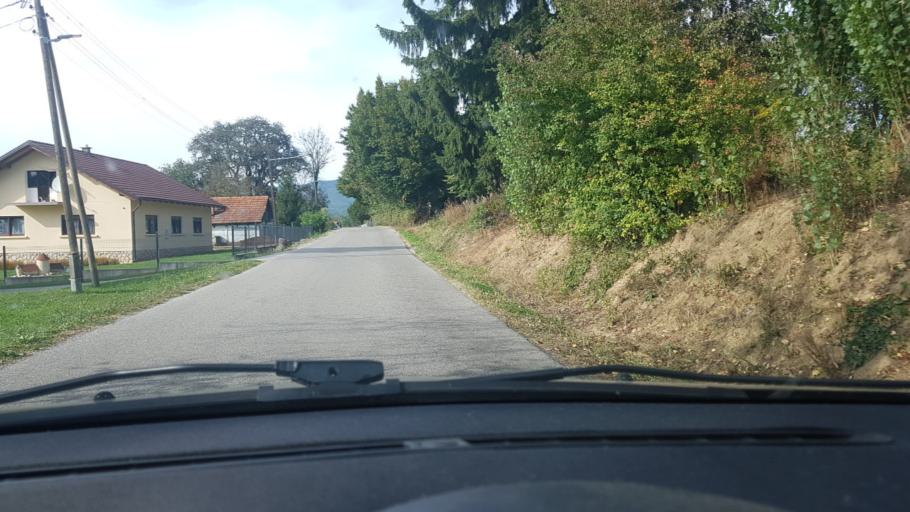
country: HR
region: Krapinsko-Zagorska
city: Zlatar
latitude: 46.1066
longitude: 16.1204
